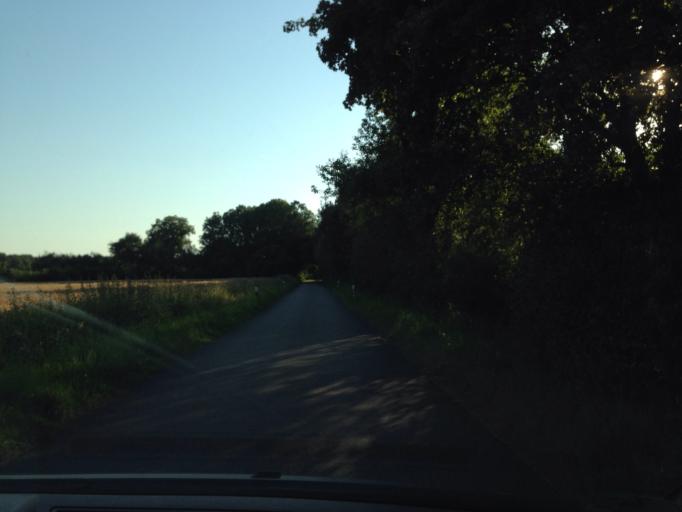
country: DE
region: North Rhine-Westphalia
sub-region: Regierungsbezirk Munster
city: Muenster
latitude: 52.0165
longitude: 7.5863
